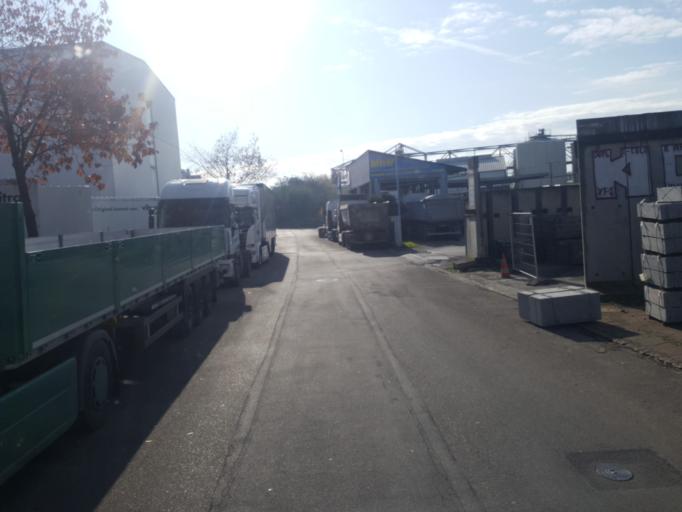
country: FR
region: Alsace
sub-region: Departement du Haut-Rhin
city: Huningue
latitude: 47.5957
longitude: 7.5943
